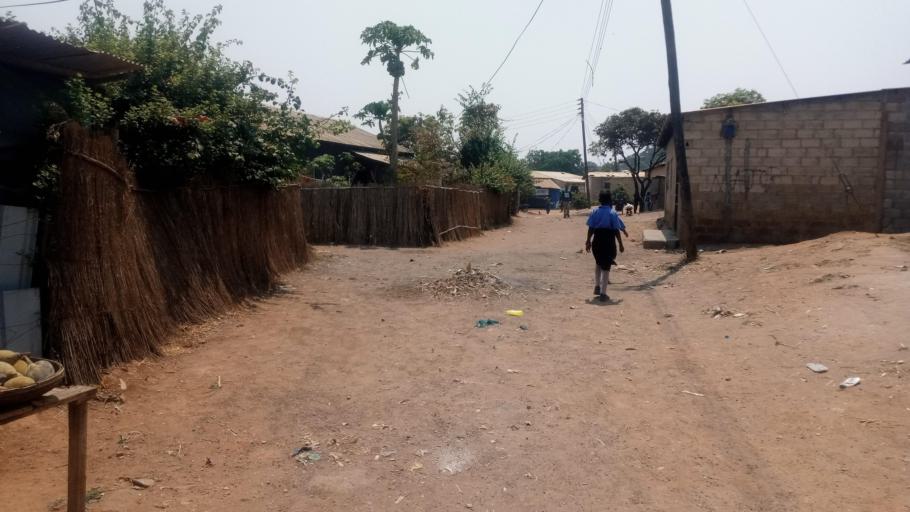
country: ZM
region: Lusaka
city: Lusaka
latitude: -15.4449
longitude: 28.3828
